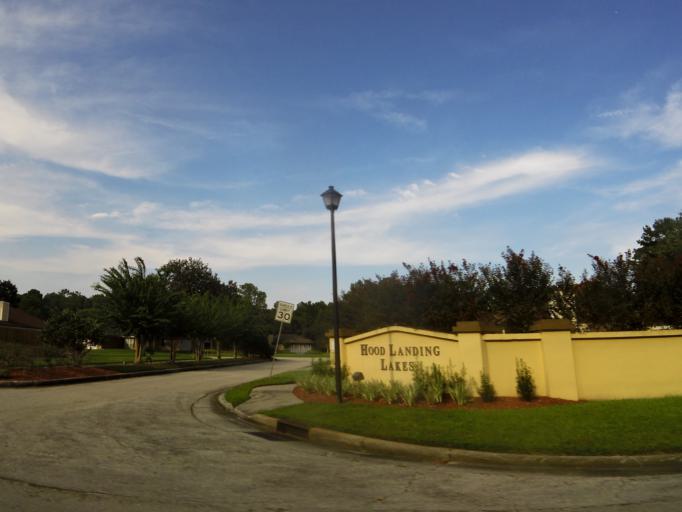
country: US
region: Florida
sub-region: Saint Johns County
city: Fruit Cove
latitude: 30.1504
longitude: -81.5964
